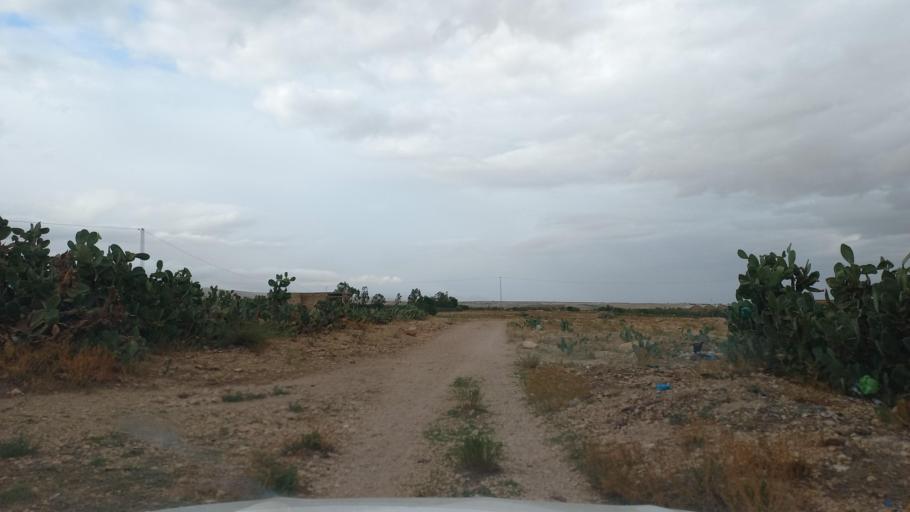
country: TN
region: Al Qasrayn
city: Kasserine
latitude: 35.2789
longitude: 8.9520
